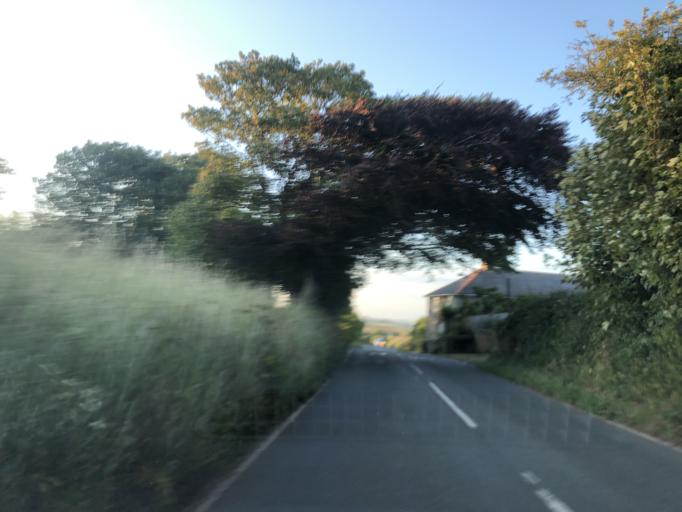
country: GB
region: England
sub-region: Isle of Wight
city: Niton
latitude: 50.6070
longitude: -1.2790
